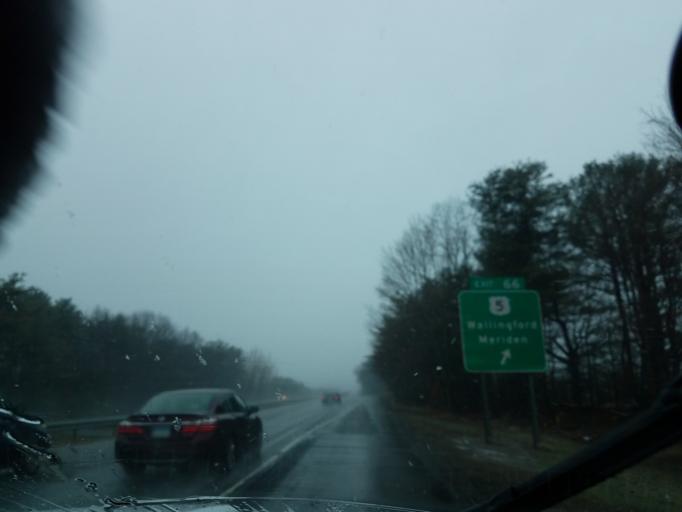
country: US
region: Connecticut
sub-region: New Haven County
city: Wallingford
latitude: 41.4945
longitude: -72.8055
